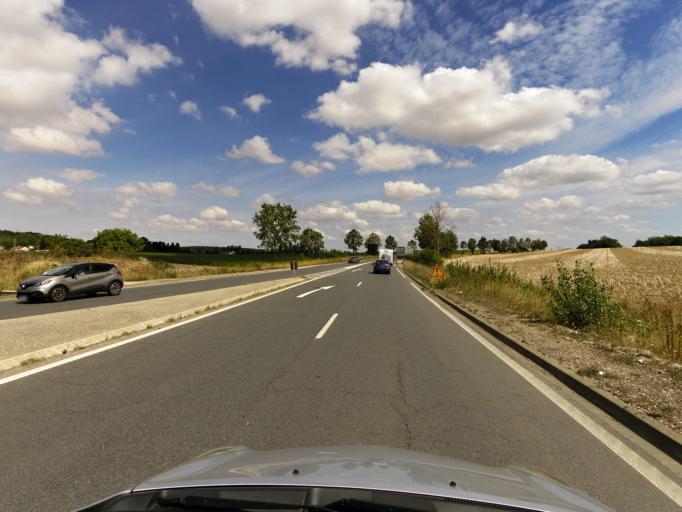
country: FR
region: Ile-de-France
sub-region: Departement de Seine-et-Marne
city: Cregy-les-Meaux
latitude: 48.9792
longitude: 2.8633
